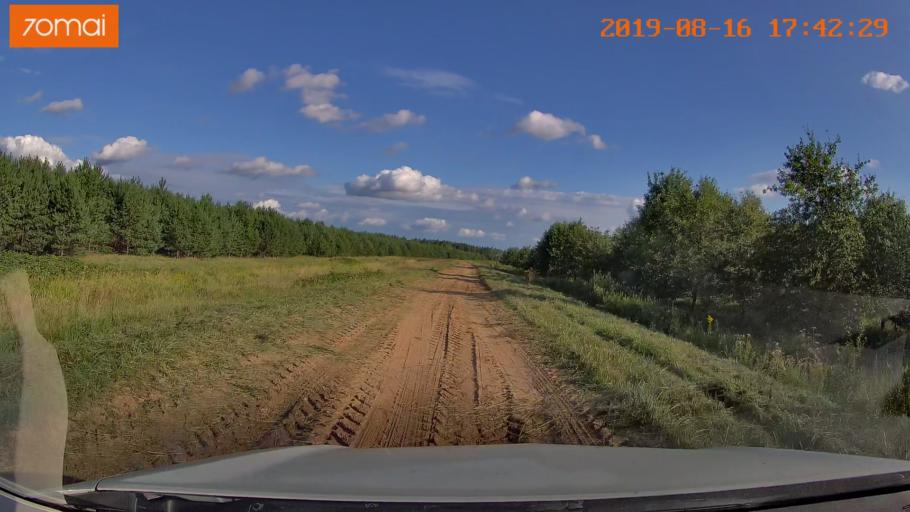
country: BY
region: Mogilev
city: Asipovichy
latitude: 53.2359
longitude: 28.6663
